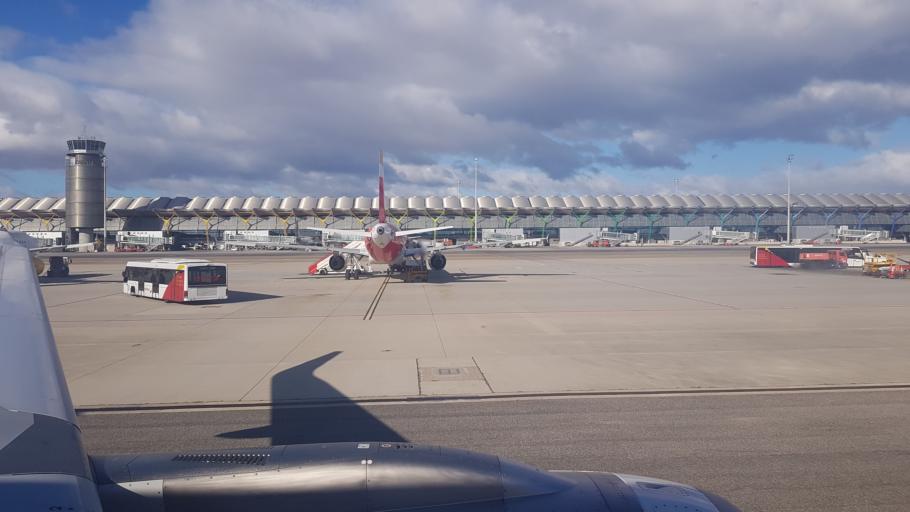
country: ES
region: Madrid
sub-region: Provincia de Madrid
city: Barajas de Madrid
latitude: 40.4935
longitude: -3.5865
